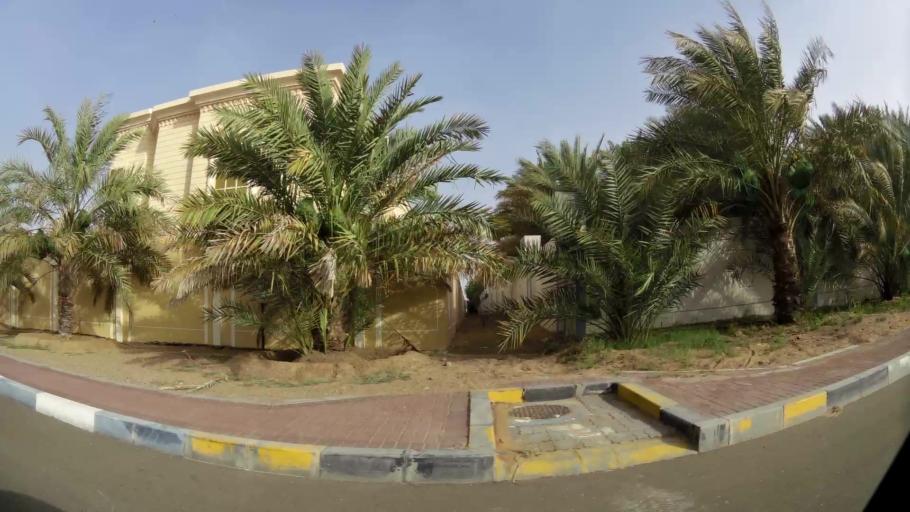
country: AE
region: Abu Dhabi
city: Al Ain
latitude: 24.2209
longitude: 55.6516
